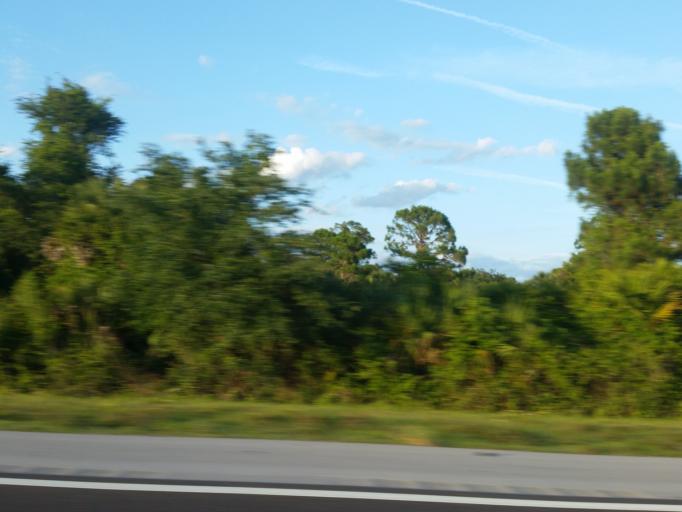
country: US
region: Florida
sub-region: Sarasota County
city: Nokomis
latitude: 27.1258
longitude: -82.3980
